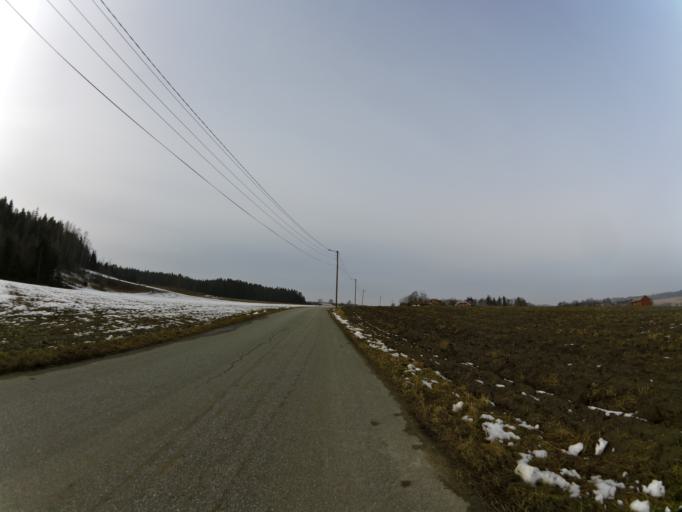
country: NO
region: Ostfold
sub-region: Fredrikstad
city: Fredrikstad
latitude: 59.2752
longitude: 11.0031
